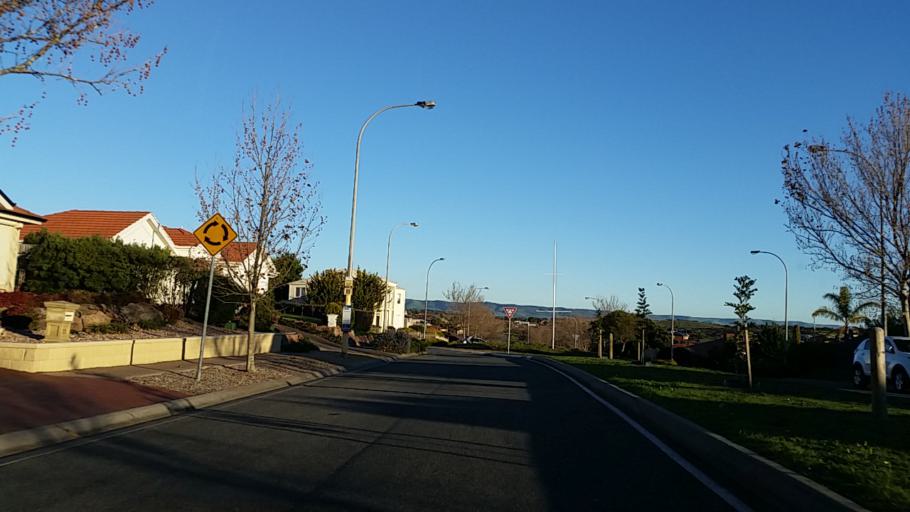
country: AU
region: South Australia
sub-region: Onkaparinga
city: Moana
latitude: -35.2034
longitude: 138.4877
